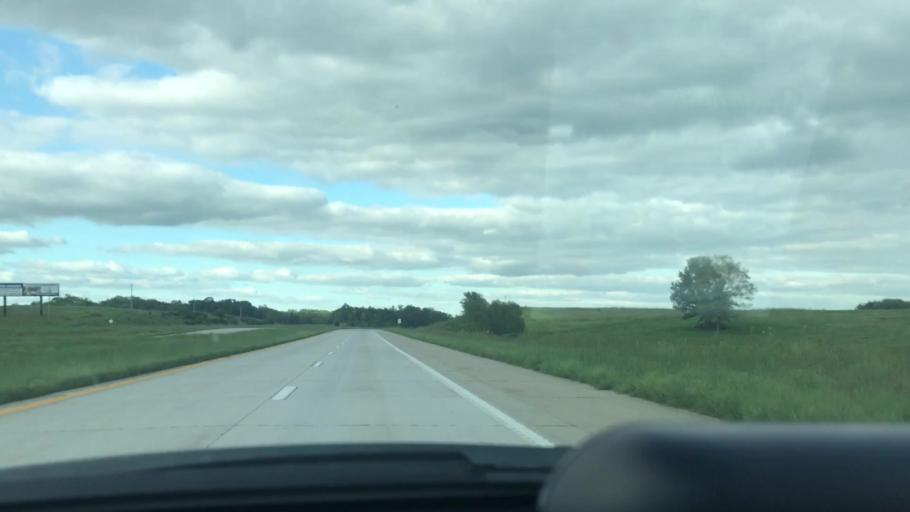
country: US
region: Missouri
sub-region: Benton County
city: Lincoln
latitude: 38.4434
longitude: -93.2945
